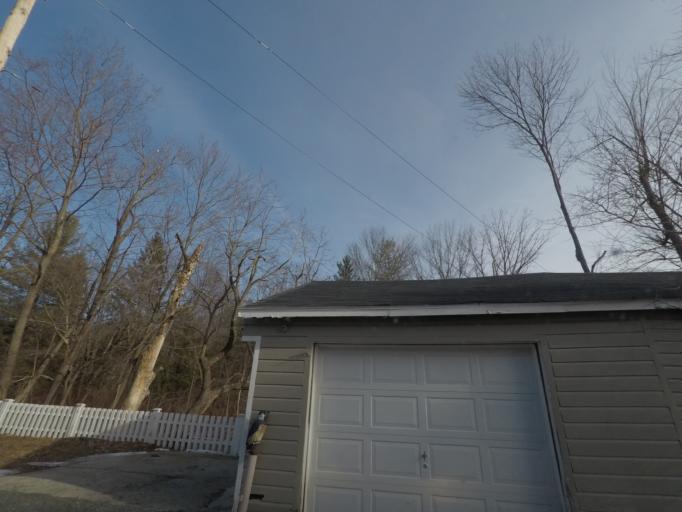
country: US
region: New York
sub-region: Rensselaer County
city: Nassau
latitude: 42.5426
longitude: -73.5989
